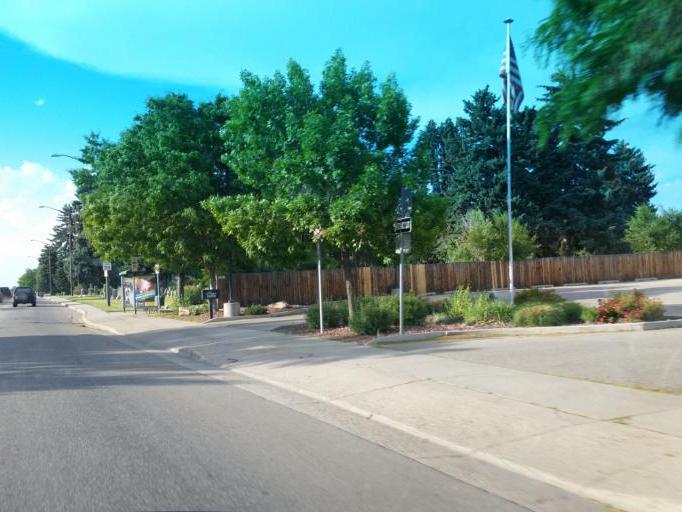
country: US
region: Colorado
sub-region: Larimer County
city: Loveland
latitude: 40.4105
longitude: -105.0730
